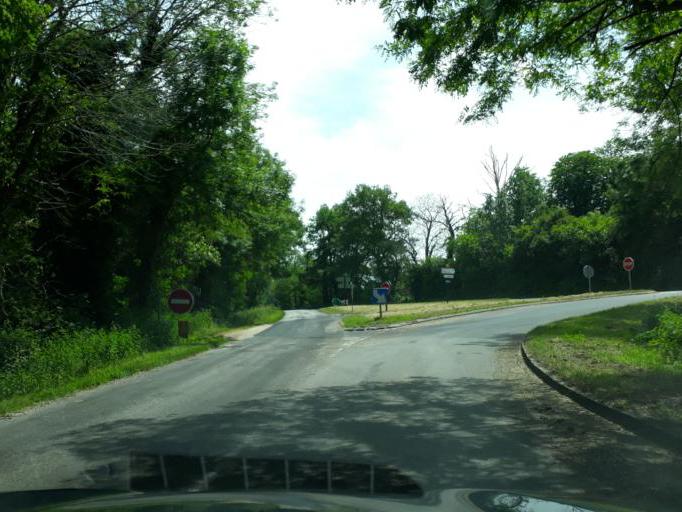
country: FR
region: Centre
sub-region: Departement du Loiret
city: Sandillon
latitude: 47.8108
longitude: 2.0520
